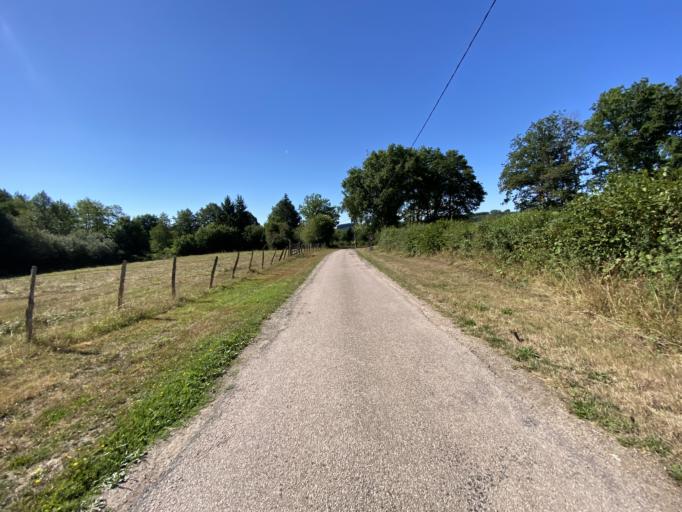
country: FR
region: Bourgogne
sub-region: Departement de la Cote-d'Or
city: Saulieu
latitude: 47.2768
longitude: 4.1789
